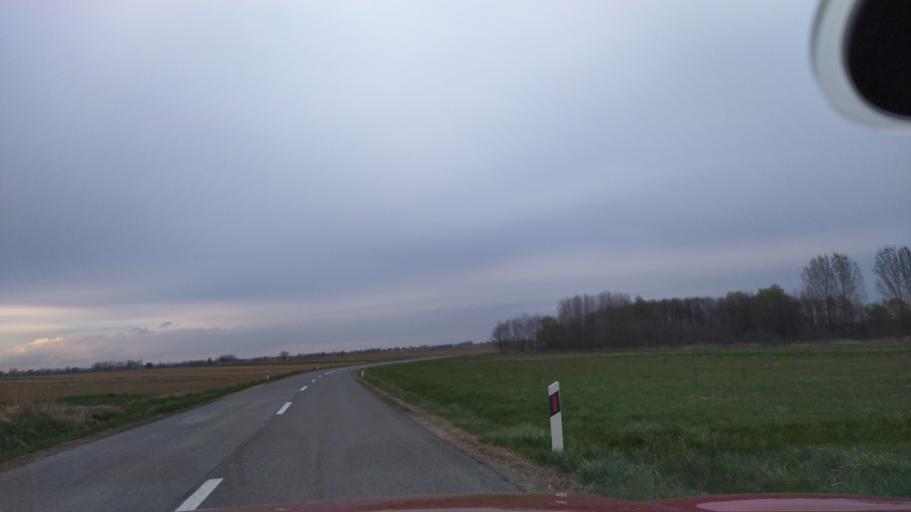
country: HR
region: Varazdinska
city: Ludbreg
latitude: 46.2481
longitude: 16.5597
